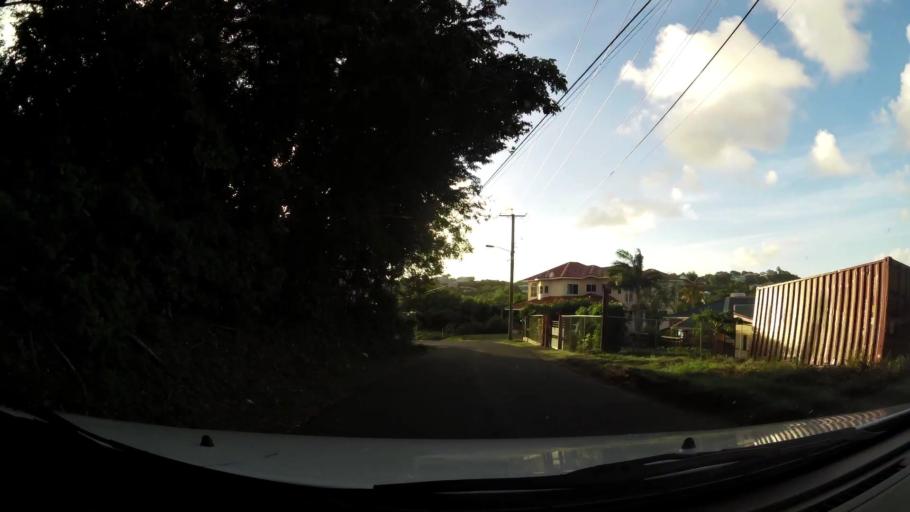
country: LC
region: Gros-Islet
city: Gros Islet
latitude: 14.0685
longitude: -60.9346
